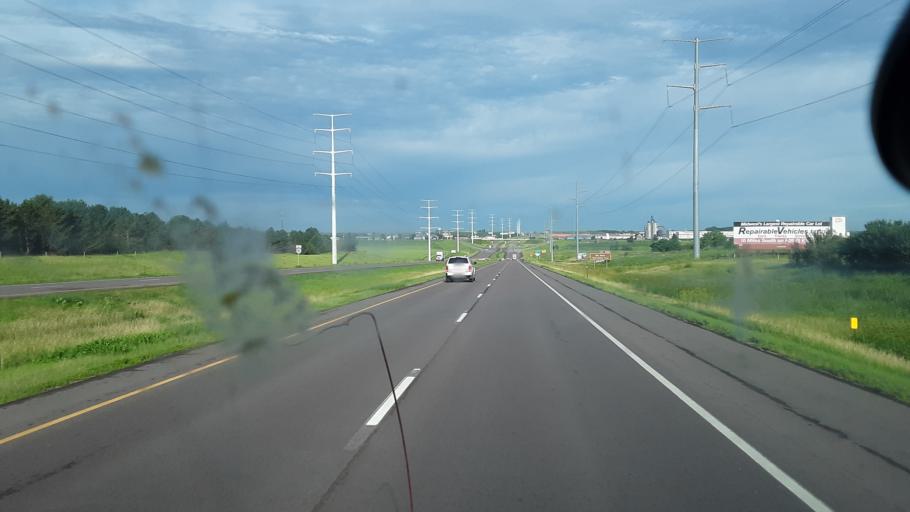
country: US
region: South Dakota
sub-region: Minnehaha County
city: Brandon
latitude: 43.6086
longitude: -96.5572
